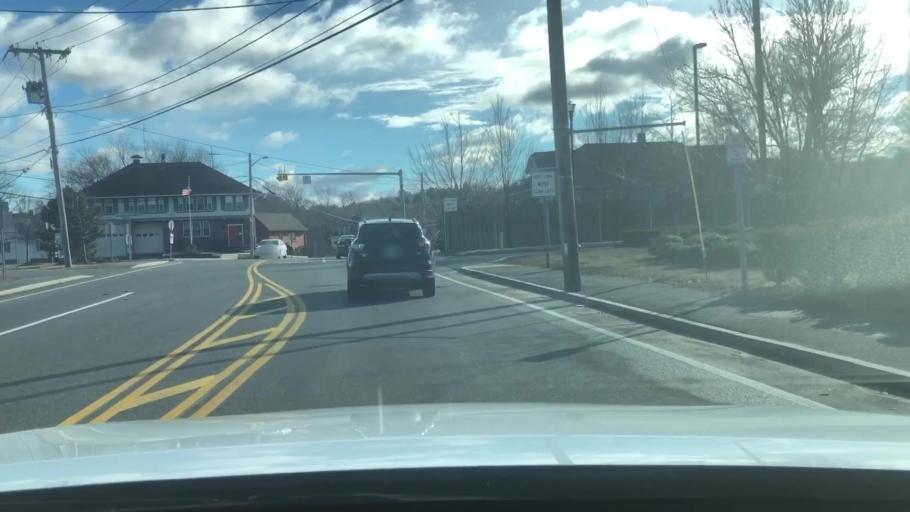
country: US
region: Rhode Island
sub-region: Providence County
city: Woonsocket
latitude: 42.0255
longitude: -71.4892
